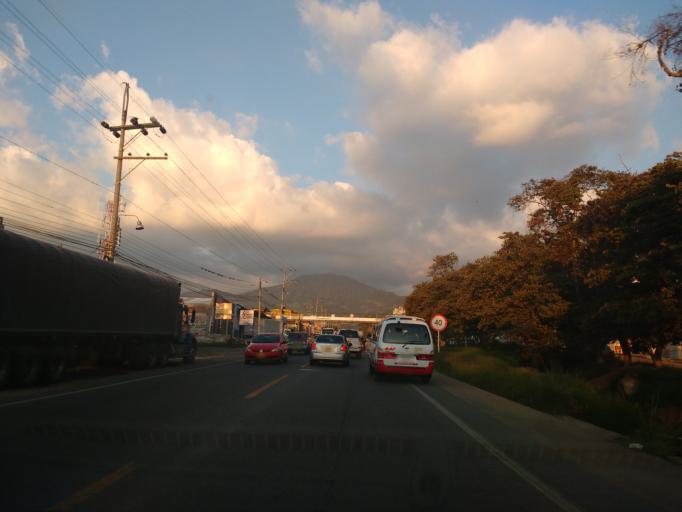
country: CO
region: Cundinamarca
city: Fusagasuga
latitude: 4.3290
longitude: -74.3858
